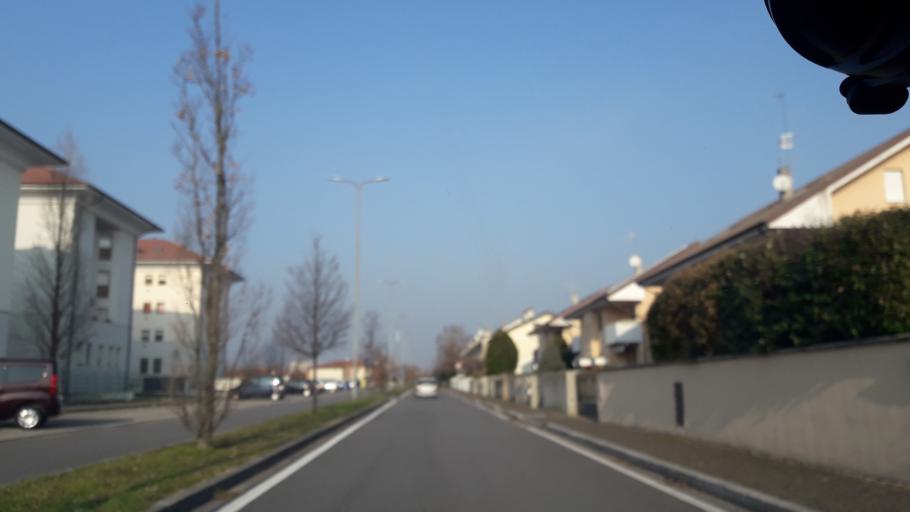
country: IT
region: Friuli Venezia Giulia
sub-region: Provincia di Udine
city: Basaldella
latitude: 46.0428
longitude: 13.2275
